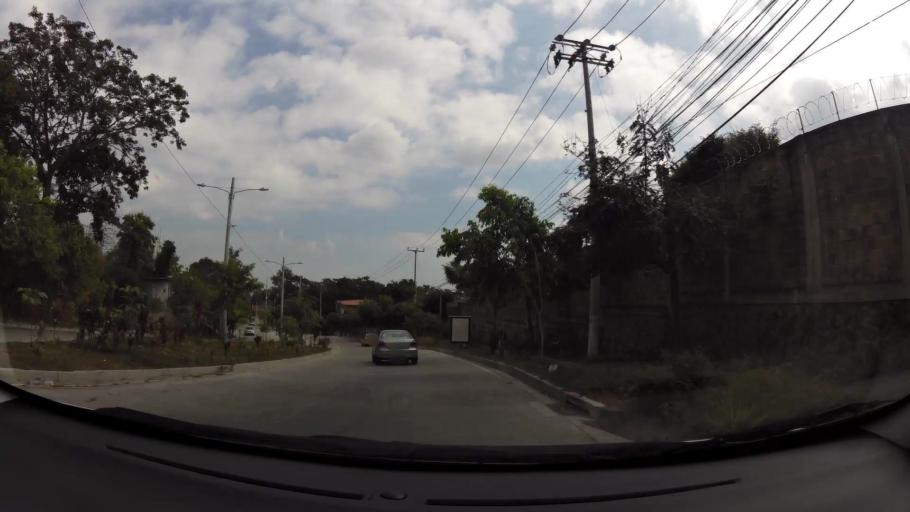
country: SV
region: San Salvador
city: Mejicanos
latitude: 13.7142
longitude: -89.2428
